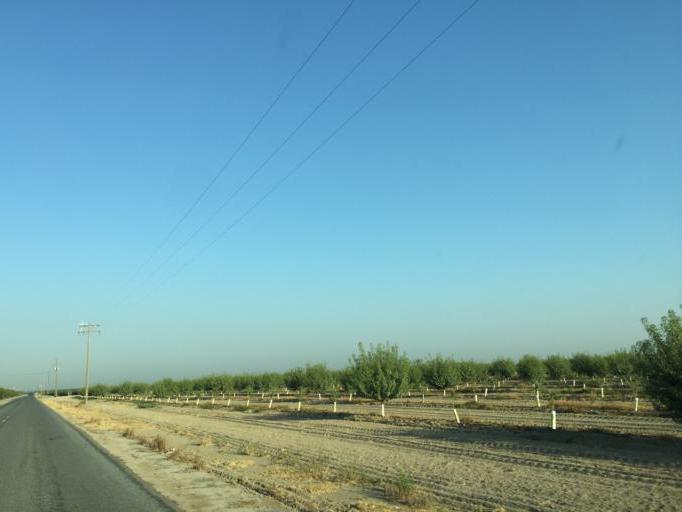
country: US
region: California
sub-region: Tulare County
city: London
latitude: 36.4585
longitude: -119.4276
